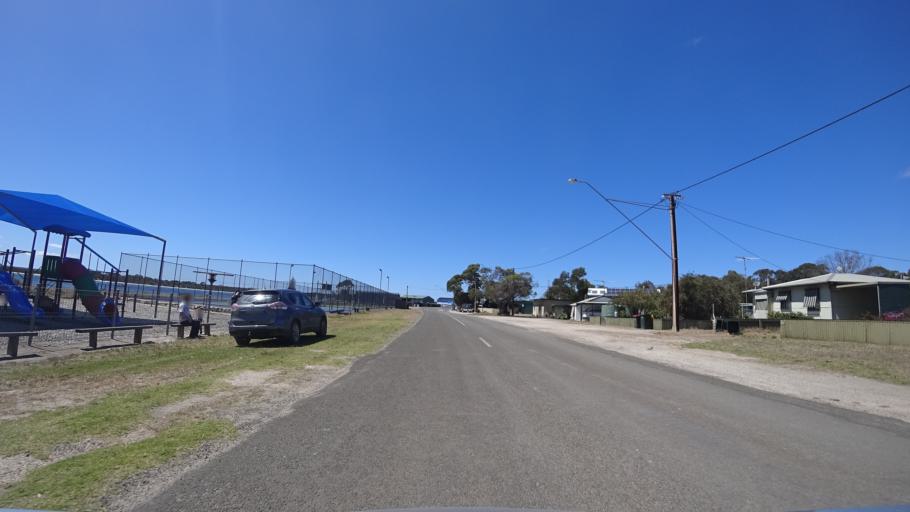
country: AU
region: South Australia
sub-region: Kangaroo Island
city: Kingscote
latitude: -35.7848
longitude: 137.7719
